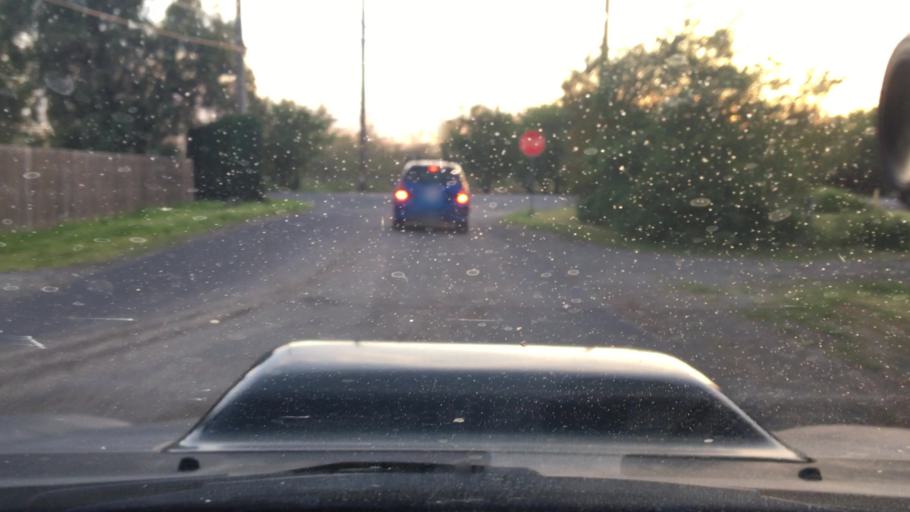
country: US
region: California
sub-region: Butte County
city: Chico
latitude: 39.7076
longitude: -121.8461
